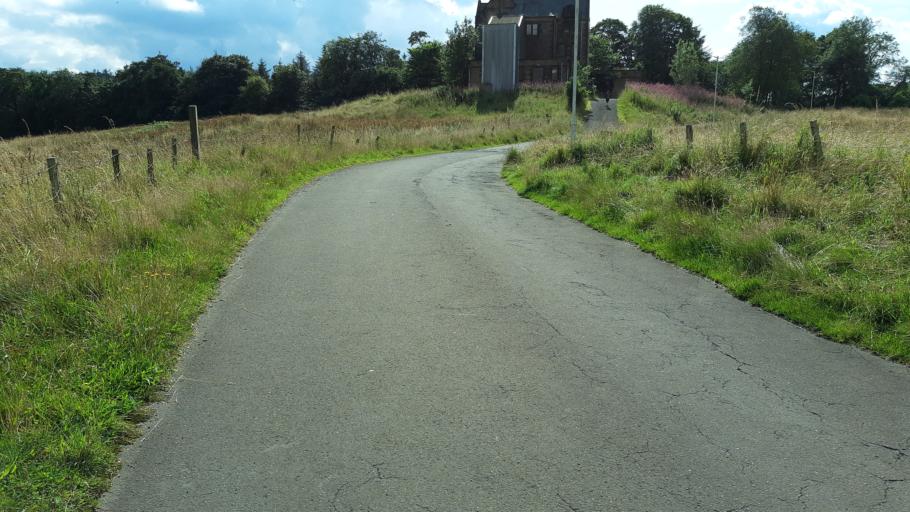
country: GB
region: Scotland
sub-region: West Lothian
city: Livingston
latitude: 55.9180
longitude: -3.5577
